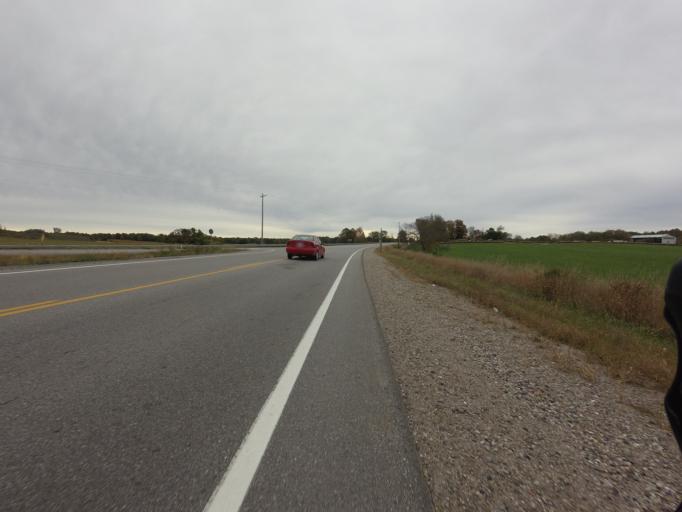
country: CA
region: Ontario
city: Gananoque
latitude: 44.4796
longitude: -76.2194
